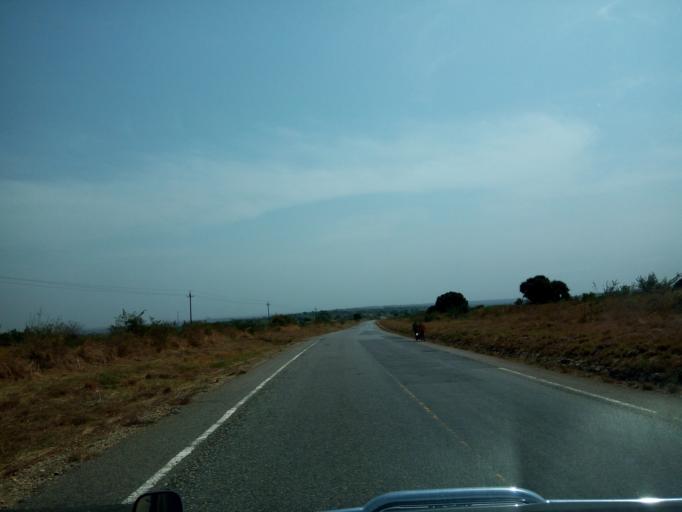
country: UG
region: Northern Region
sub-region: Nebbi District
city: Nebbi
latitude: 2.4636
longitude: 31.2983
